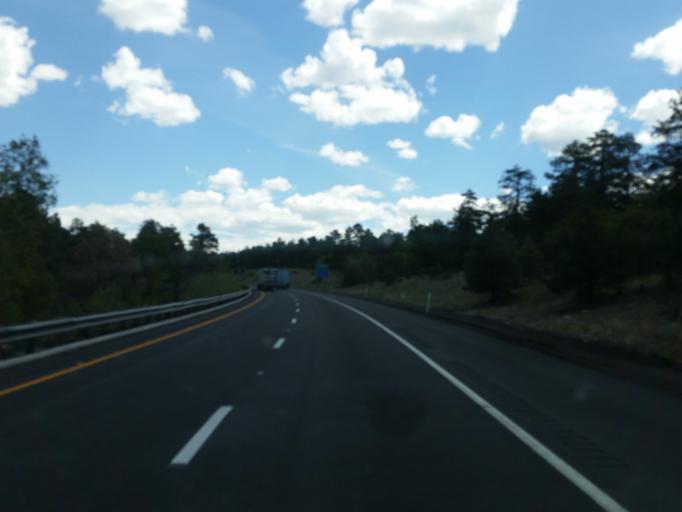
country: US
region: Arizona
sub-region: Coconino County
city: Williams
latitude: 35.2238
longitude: -112.2393
